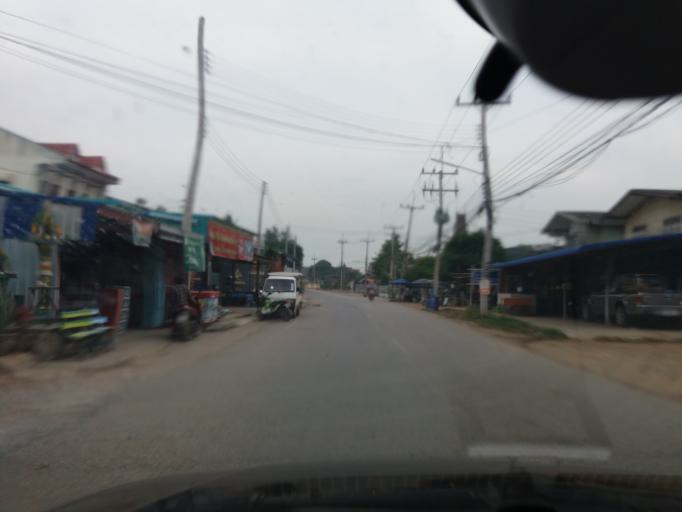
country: TH
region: Suphan Buri
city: Doembang Nangbuat
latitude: 14.8384
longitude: 100.1365
